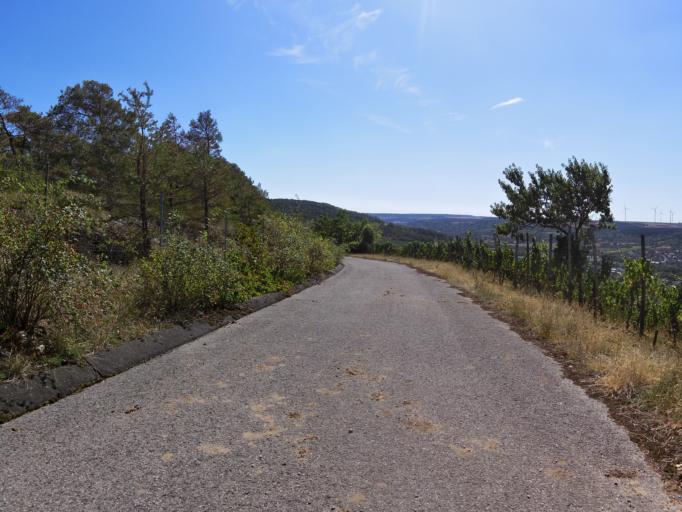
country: DE
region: Bavaria
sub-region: Regierungsbezirk Unterfranken
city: Thungersheim
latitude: 49.8711
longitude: 9.8591
